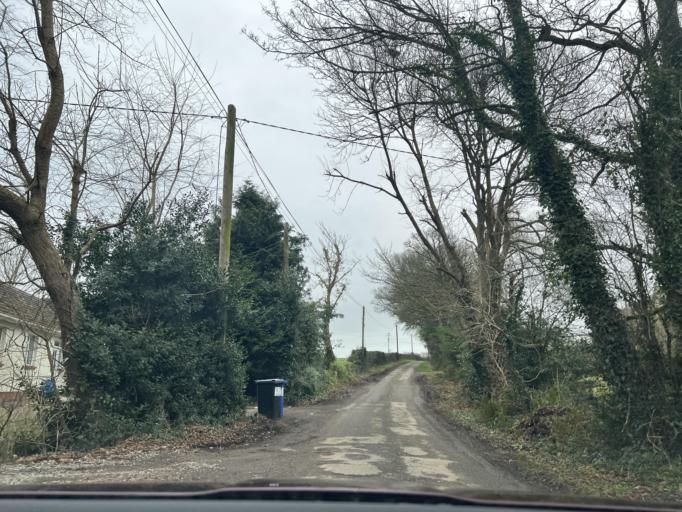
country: IE
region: Leinster
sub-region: Loch Garman
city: Castlebridge
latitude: 52.3885
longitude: -6.5422
